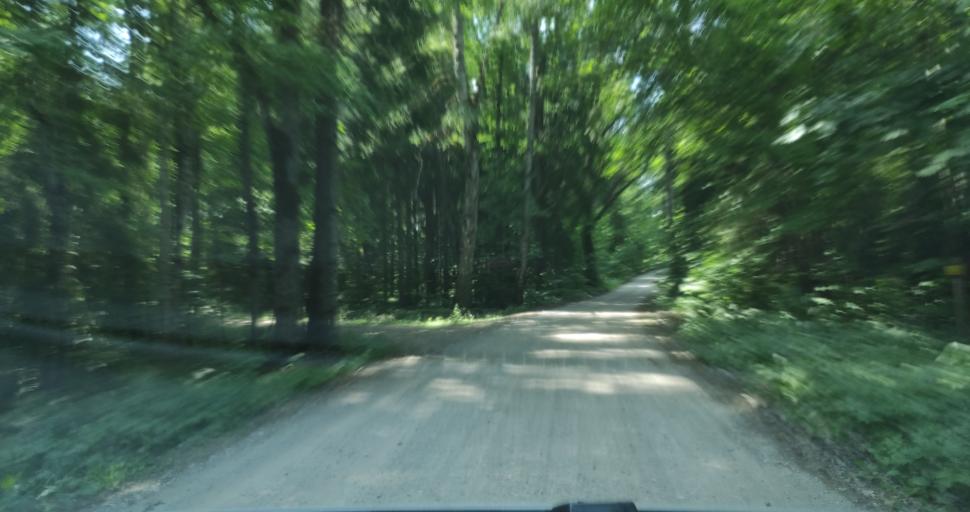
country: LV
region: Kuldigas Rajons
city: Kuldiga
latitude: 56.8478
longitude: 21.9239
